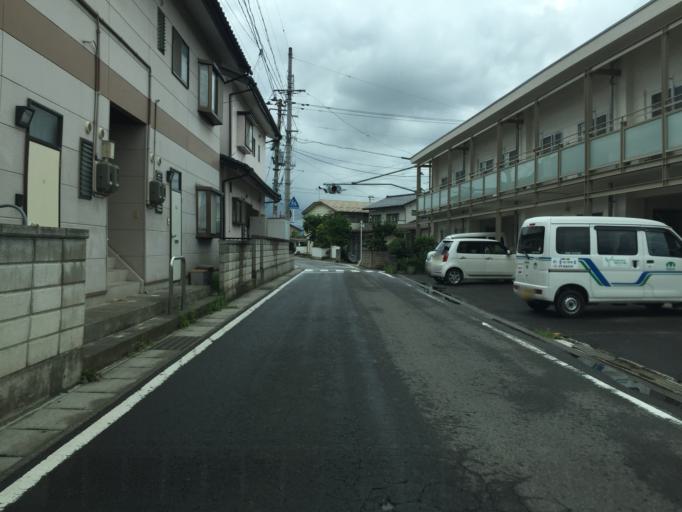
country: JP
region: Fukushima
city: Fukushima-shi
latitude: 37.7437
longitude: 140.4772
